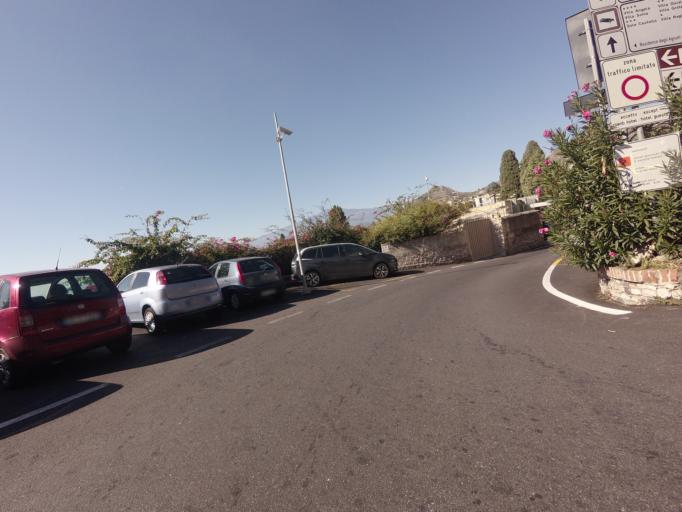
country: IT
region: Sicily
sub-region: Messina
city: Taormina
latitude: 37.8521
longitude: 15.2828
